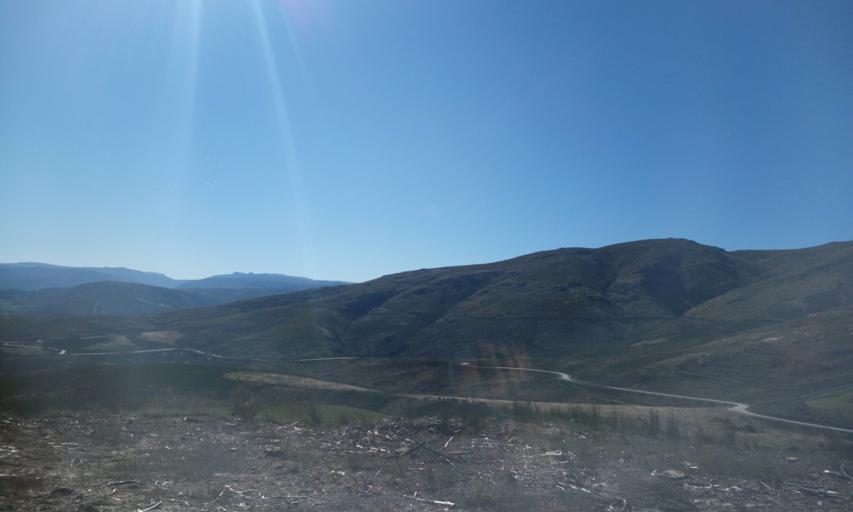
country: PT
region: Guarda
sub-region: Manteigas
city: Manteigas
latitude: 40.4787
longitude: -7.5106
